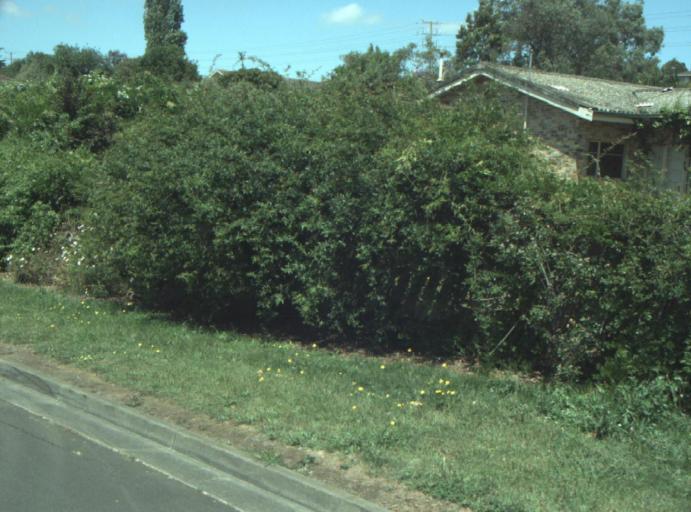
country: AU
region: Victoria
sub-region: Greater Geelong
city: Wandana Heights
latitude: -38.1695
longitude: 144.3109
